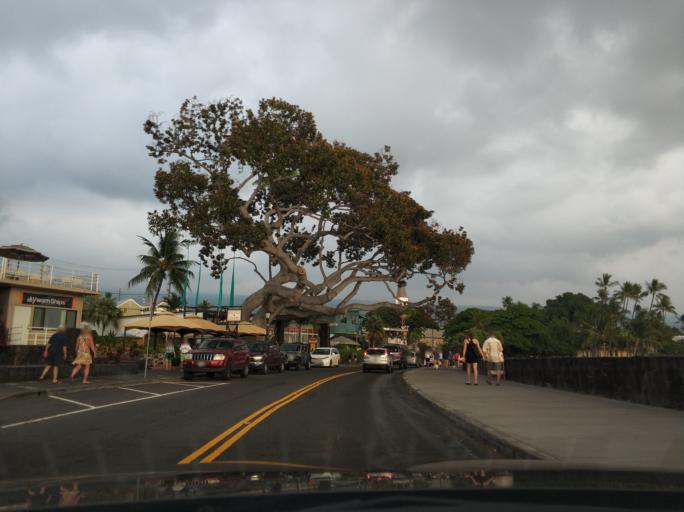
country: US
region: Hawaii
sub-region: Hawaii County
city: Kailua-Kona
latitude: 19.6402
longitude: -155.9958
